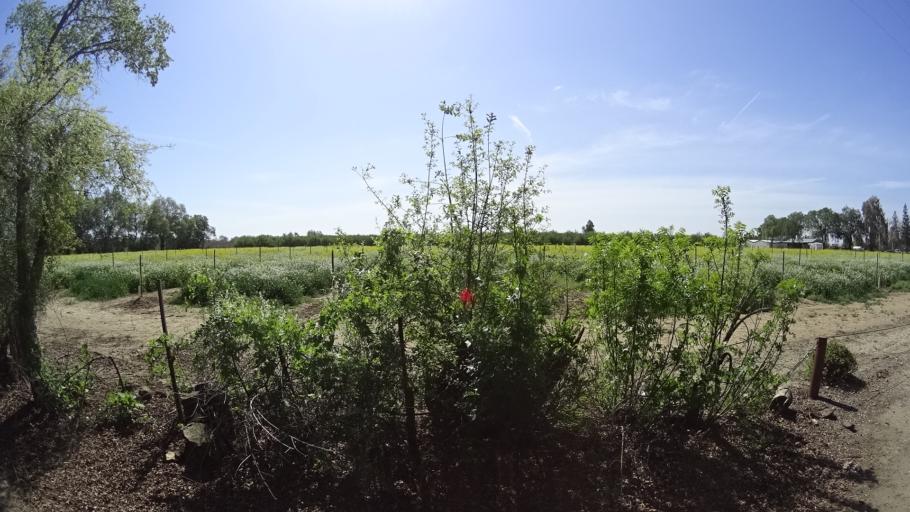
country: US
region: California
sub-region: Glenn County
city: Hamilton City
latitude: 39.7862
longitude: -122.0443
